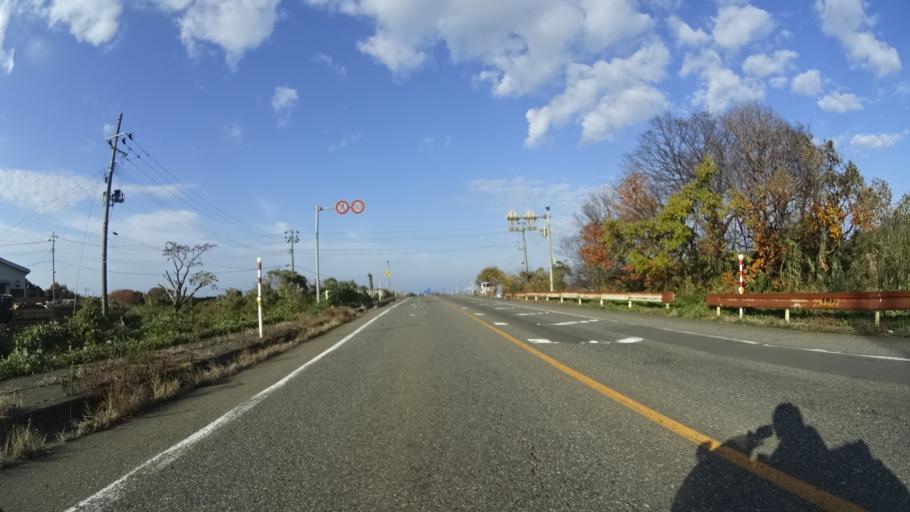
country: JP
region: Niigata
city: Kashiwazaki
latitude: 37.3268
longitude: 138.4557
